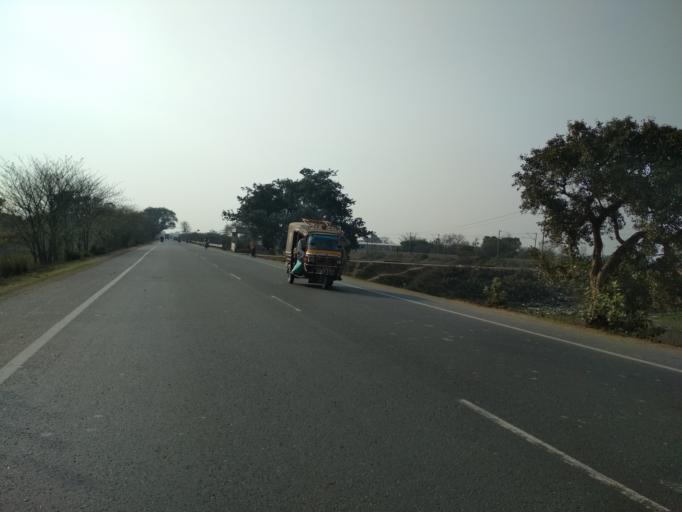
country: IN
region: Bihar
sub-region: Khagaria
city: Khagaria
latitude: 25.5080
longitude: 86.5421
